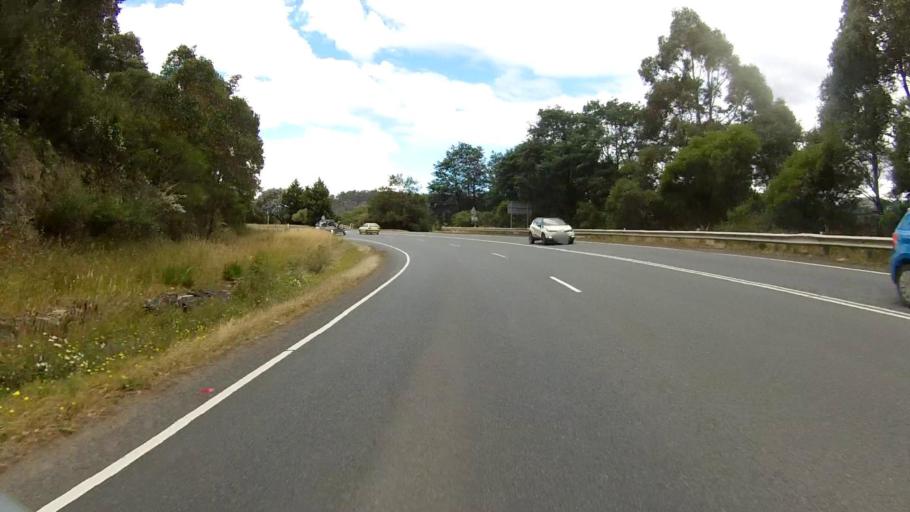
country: AU
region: Tasmania
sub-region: Huon Valley
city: Huonville
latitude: -42.9755
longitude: 147.1478
